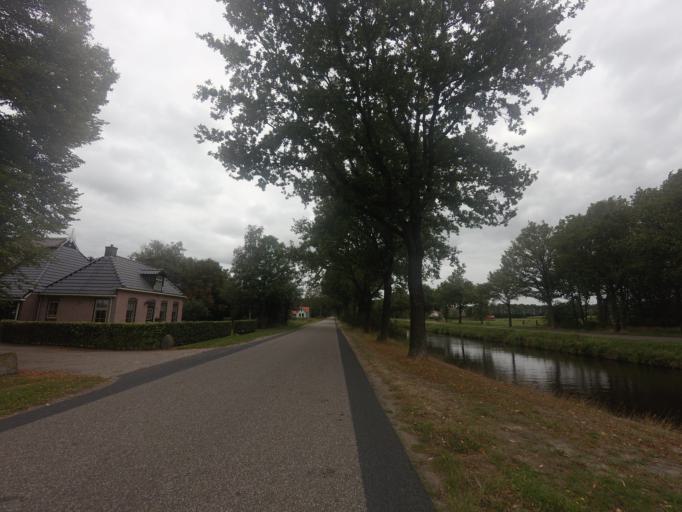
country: NL
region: Drenthe
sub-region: Gemeente Westerveld
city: Dwingeloo
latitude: 52.9731
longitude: 6.3244
